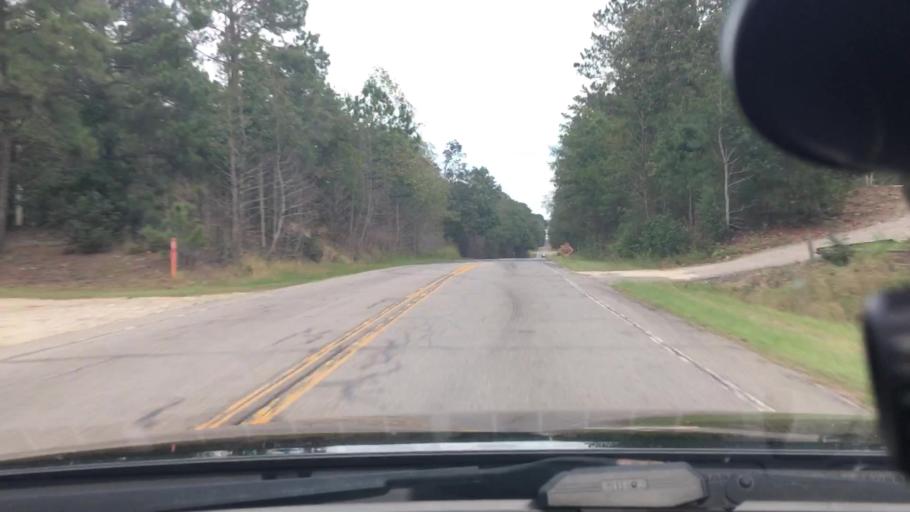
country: US
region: North Carolina
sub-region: Moore County
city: Carthage
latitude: 35.3476
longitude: -79.3796
